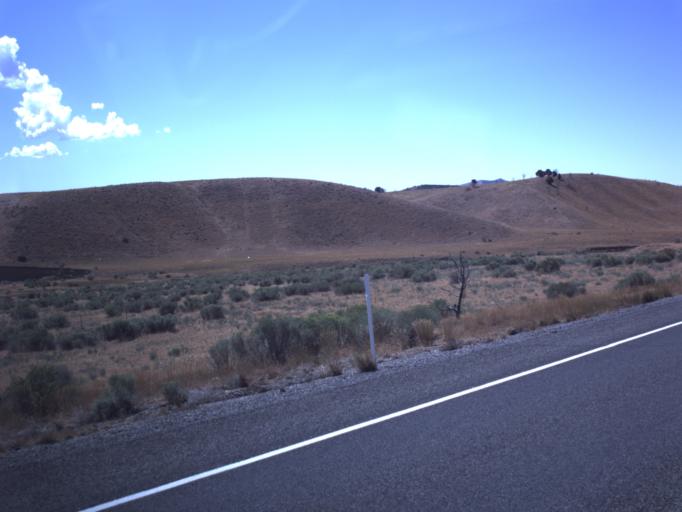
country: US
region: Utah
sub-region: Juab County
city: Nephi
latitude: 39.6396
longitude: -112.0914
